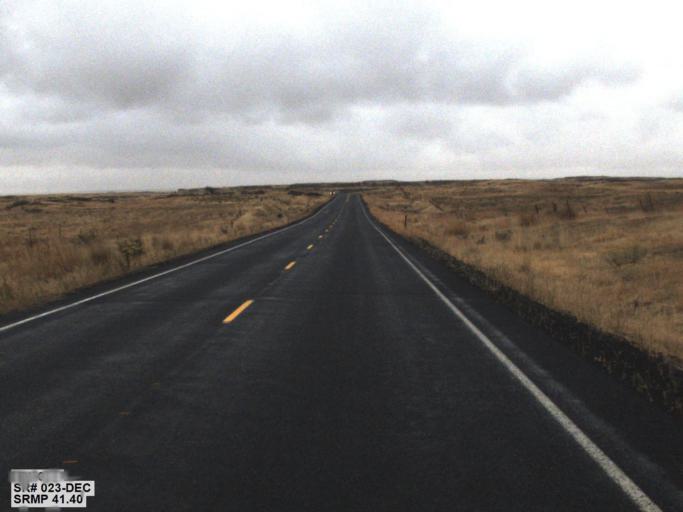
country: US
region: Washington
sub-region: Spokane County
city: Medical Lake
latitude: 47.2789
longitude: -117.9576
